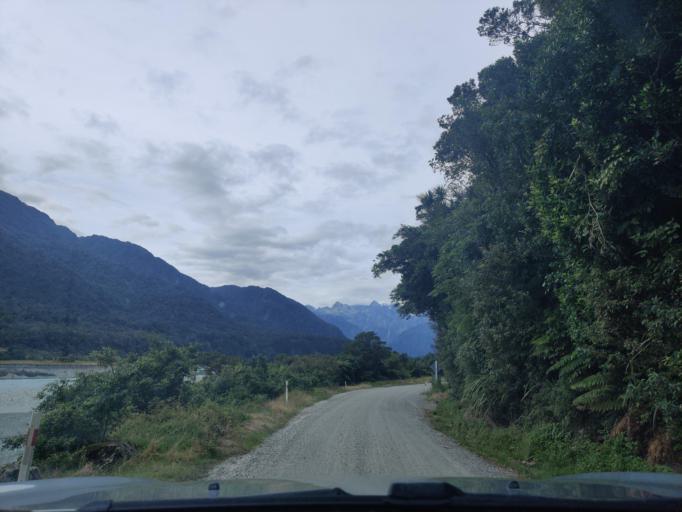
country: NZ
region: West Coast
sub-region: Westland District
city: Hokitika
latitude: -43.2877
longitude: 170.4042
